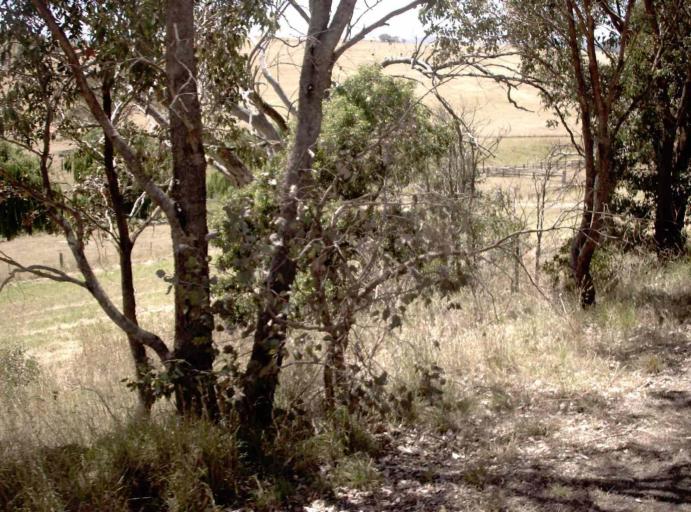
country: AU
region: Victoria
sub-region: East Gippsland
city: Bairnsdale
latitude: -37.1762
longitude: 147.7015
